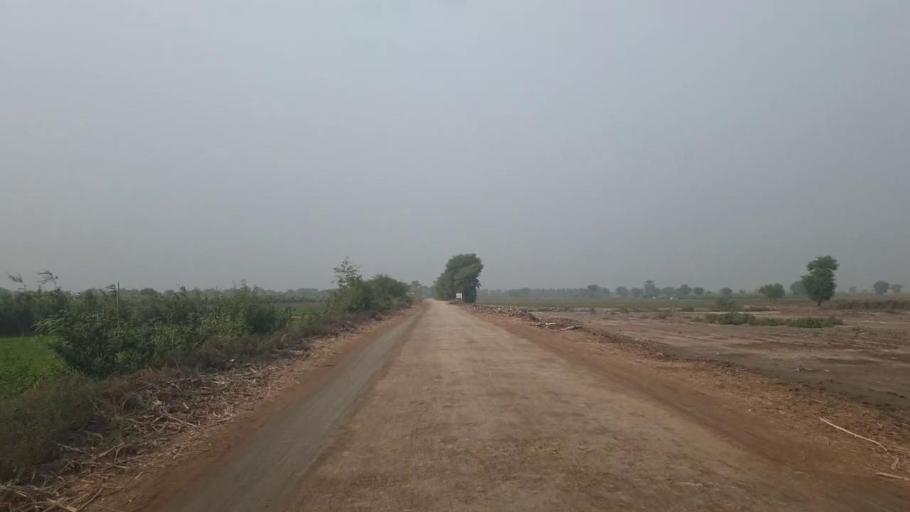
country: PK
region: Sindh
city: Tando Adam
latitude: 25.8093
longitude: 68.7191
